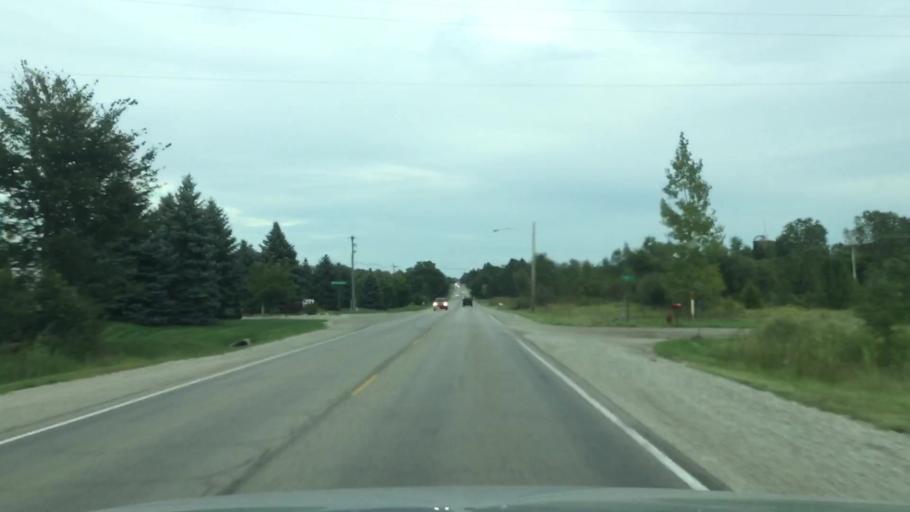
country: US
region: Michigan
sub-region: Genesee County
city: Lake Fenton
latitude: 42.8860
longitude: -83.6720
